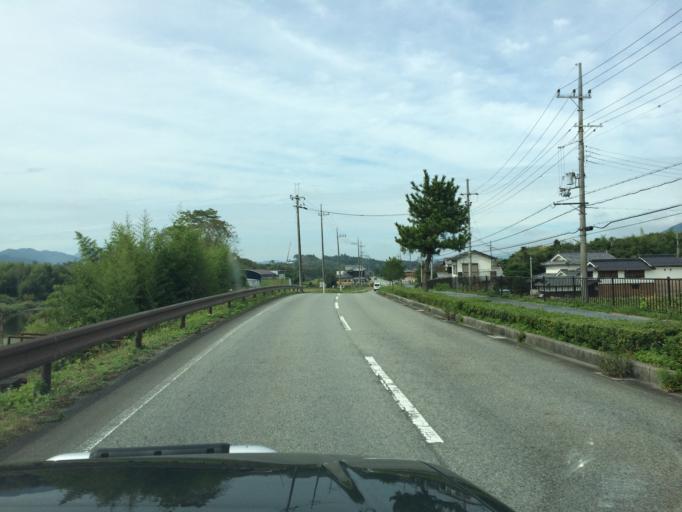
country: JP
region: Hyogo
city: Sasayama
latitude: 35.0729
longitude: 135.2463
